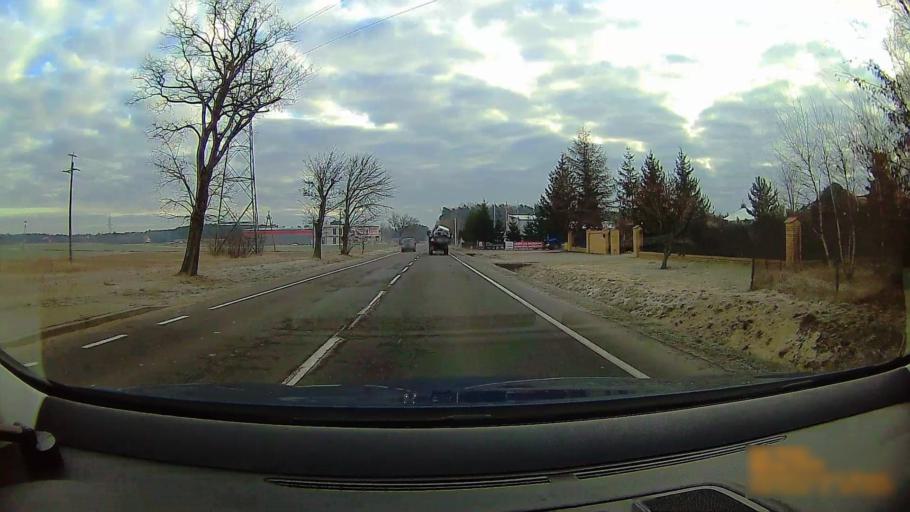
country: PL
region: Greater Poland Voivodeship
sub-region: Powiat koninski
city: Stare Miasto
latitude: 52.2016
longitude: 18.1986
